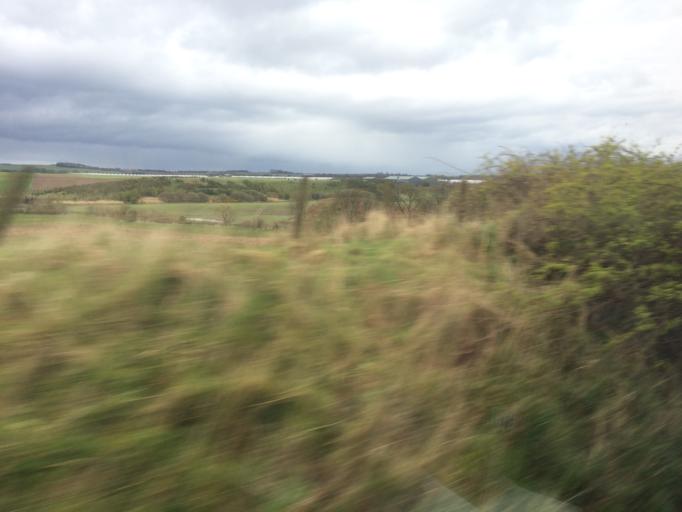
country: GB
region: Scotland
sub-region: Angus
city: Montrose
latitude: 56.6496
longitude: -2.5314
